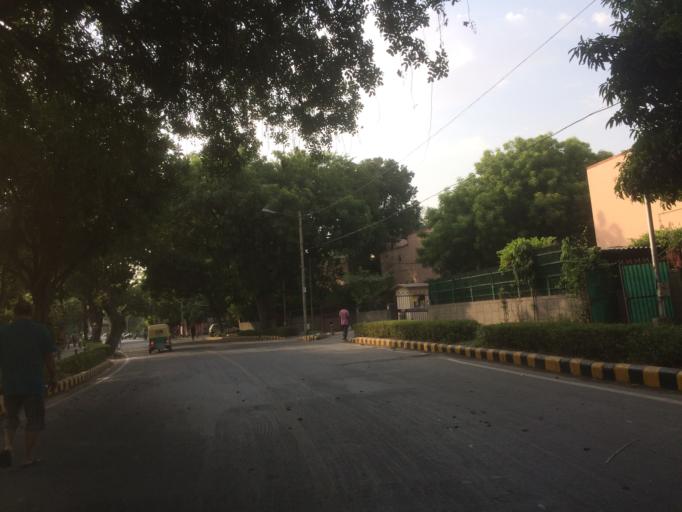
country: IN
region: NCT
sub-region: New Delhi
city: New Delhi
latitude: 28.5760
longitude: 77.2064
